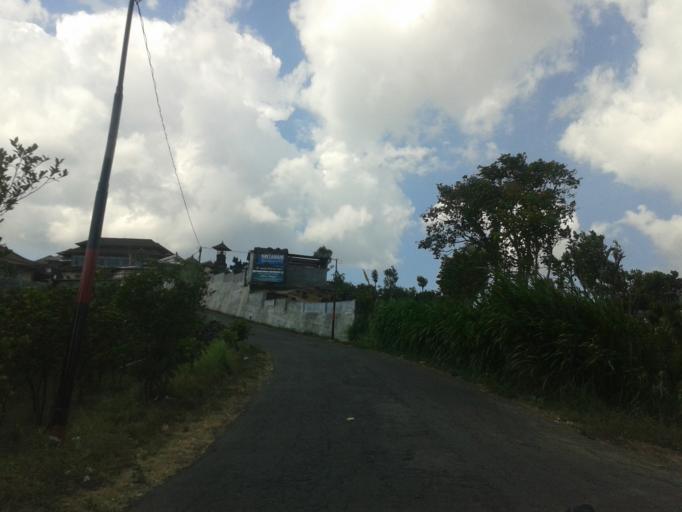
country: ID
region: Bali
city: Banjar Kedisan
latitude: -8.2791
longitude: 115.3510
